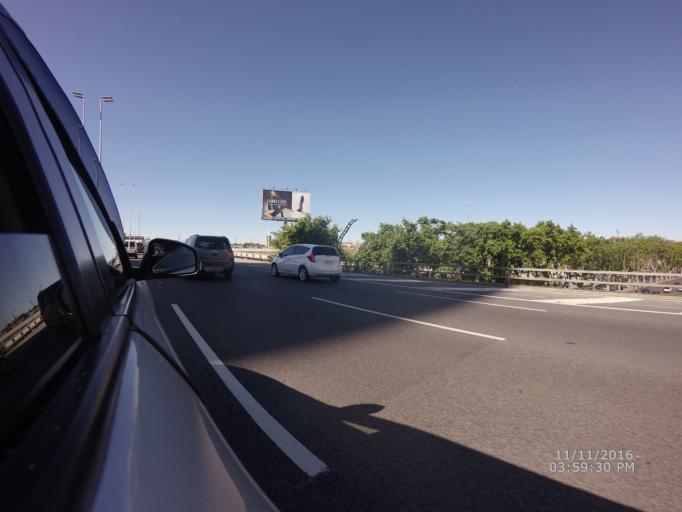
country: AR
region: Buenos Aires F.D.
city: Retiro
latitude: -34.5890
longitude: -58.3815
